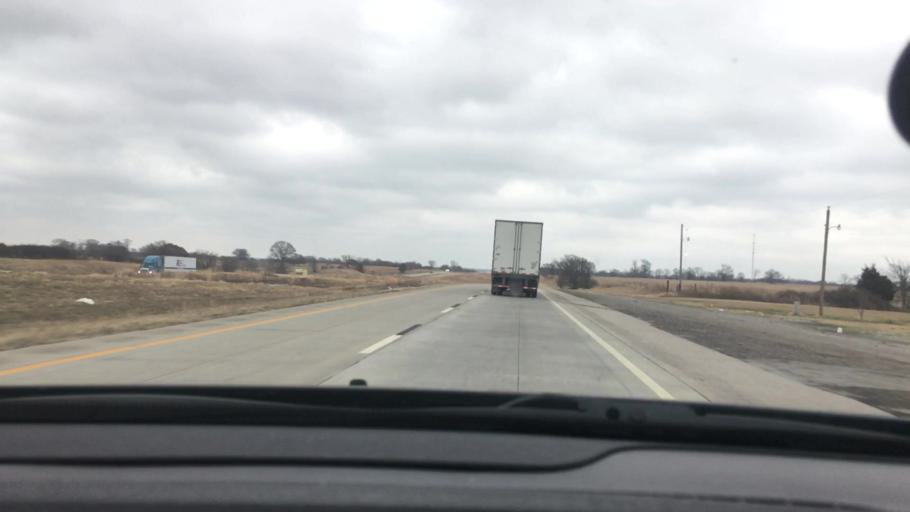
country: US
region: Oklahoma
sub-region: Atoka County
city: Atoka
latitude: 34.2162
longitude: -96.2303
